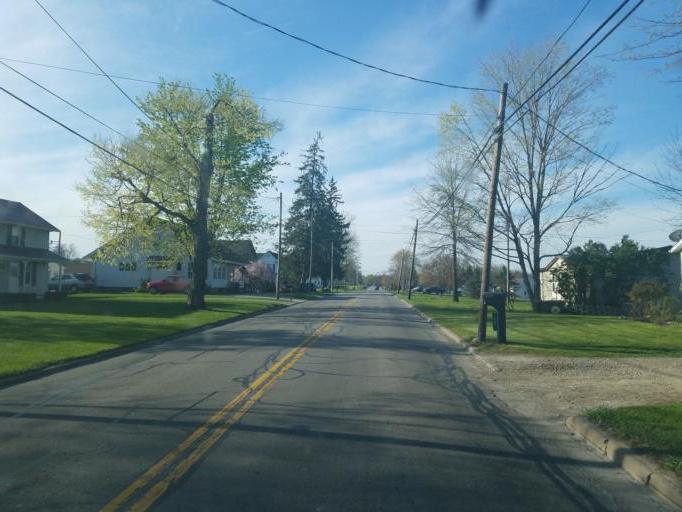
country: US
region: Ohio
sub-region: Ashland County
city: Ashland
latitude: 40.9687
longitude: -82.3648
